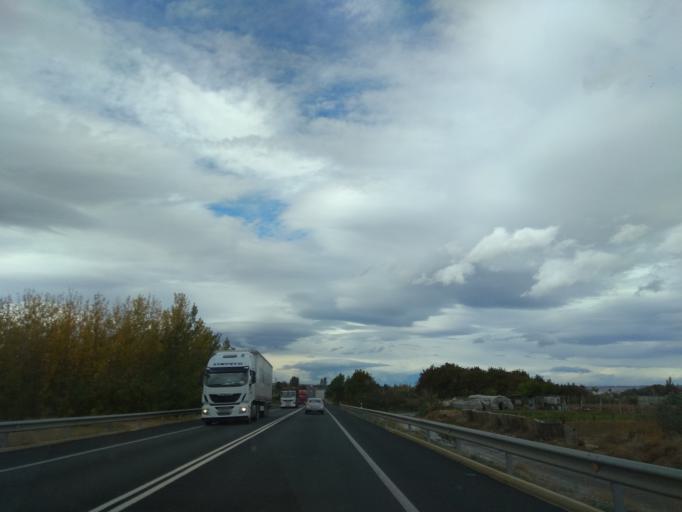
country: ES
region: La Rioja
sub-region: Provincia de La Rioja
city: Alfaro
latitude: 42.1679
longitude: -1.7550
